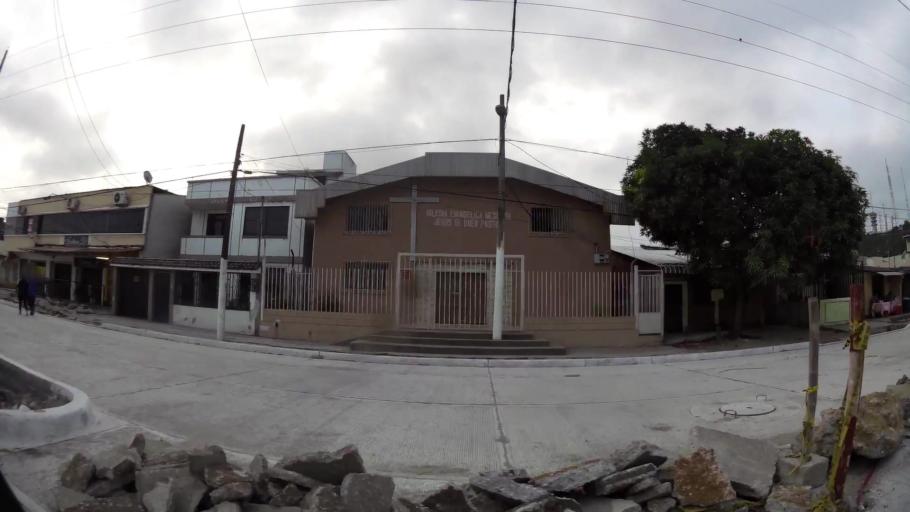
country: EC
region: Guayas
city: Eloy Alfaro
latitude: -2.1749
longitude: -79.8839
